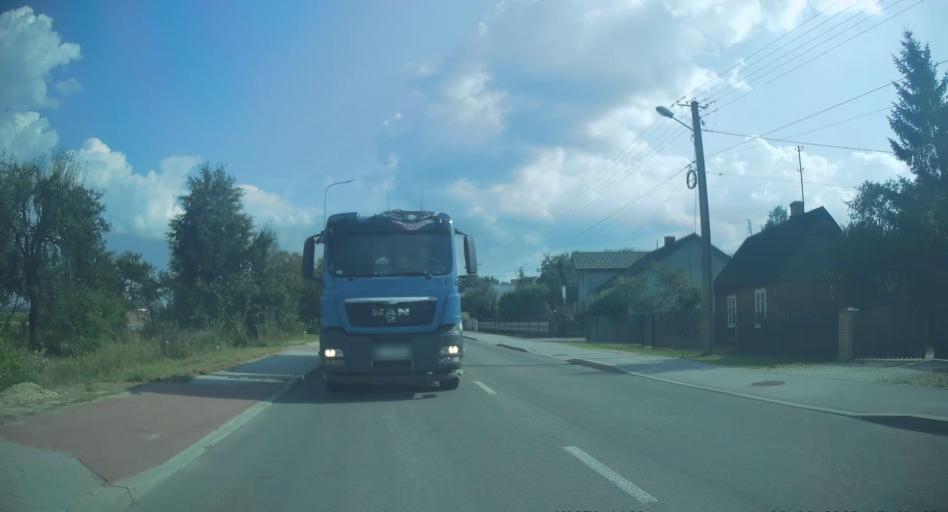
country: PL
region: Swietokrzyskie
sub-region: Powiat konecki
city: Radoszyce
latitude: 51.0505
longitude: 20.2816
